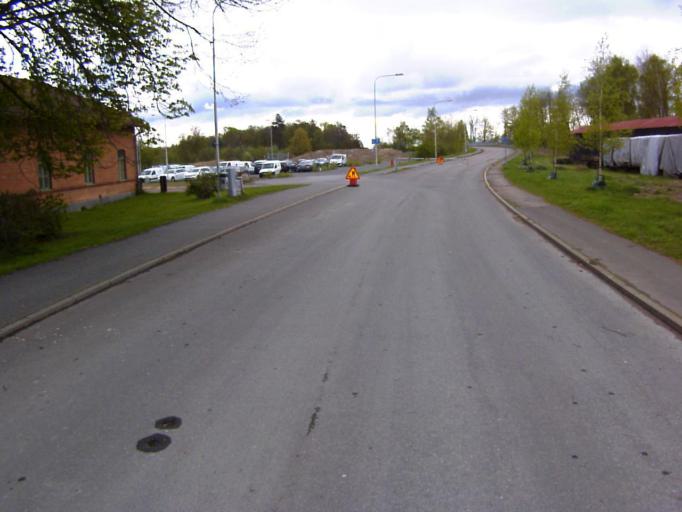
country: SE
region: Skane
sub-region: Kristianstads Kommun
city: Kristianstad
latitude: 56.0206
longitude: 14.1652
